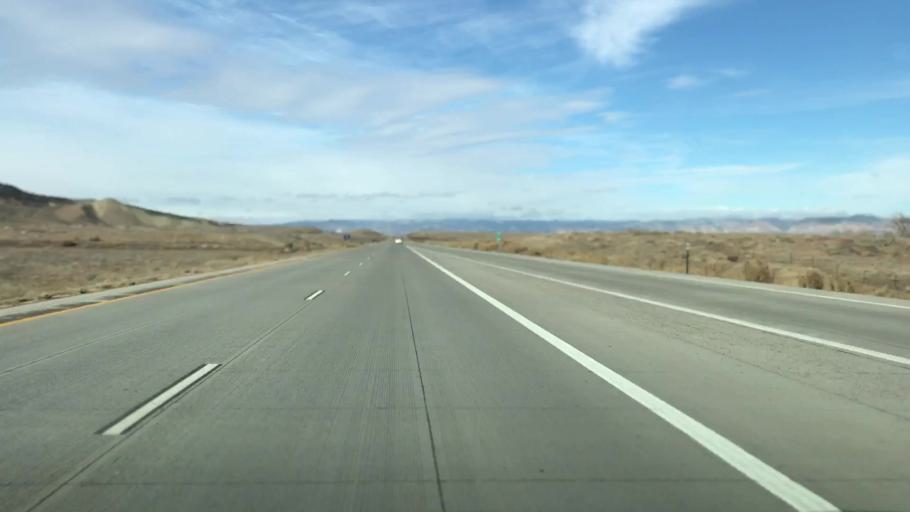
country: US
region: Colorado
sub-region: Mesa County
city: Loma
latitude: 39.1834
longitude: -108.8291
